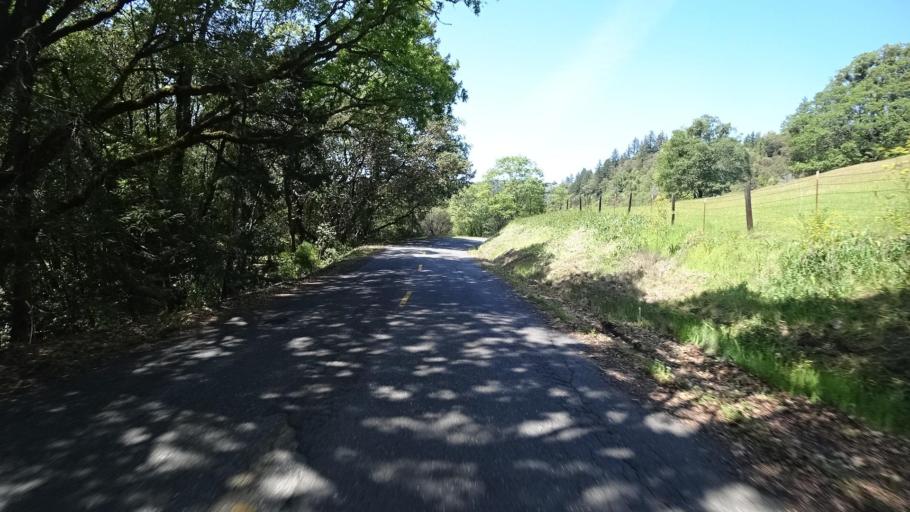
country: US
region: California
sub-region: Humboldt County
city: Redway
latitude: 40.2598
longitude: -123.6263
